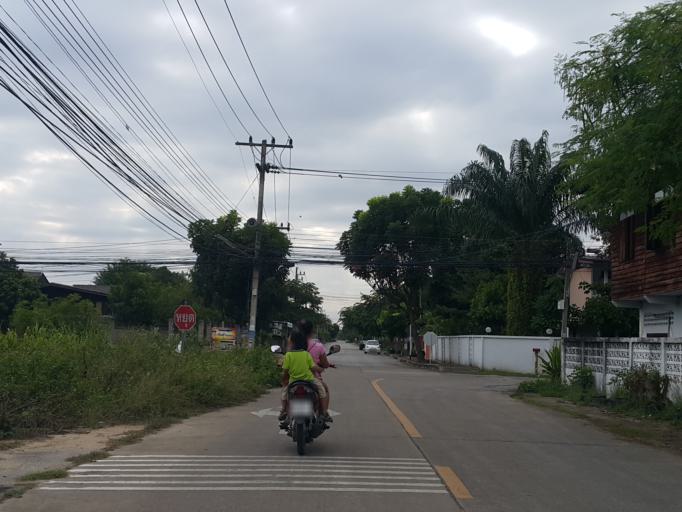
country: TH
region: Lampang
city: Lampang
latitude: 18.2774
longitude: 99.4927
